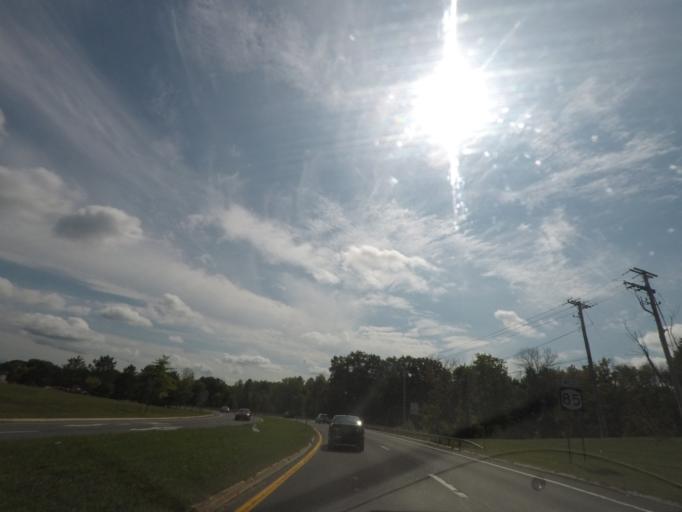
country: US
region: New York
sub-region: Albany County
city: Delmar
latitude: 42.6395
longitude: -73.8594
